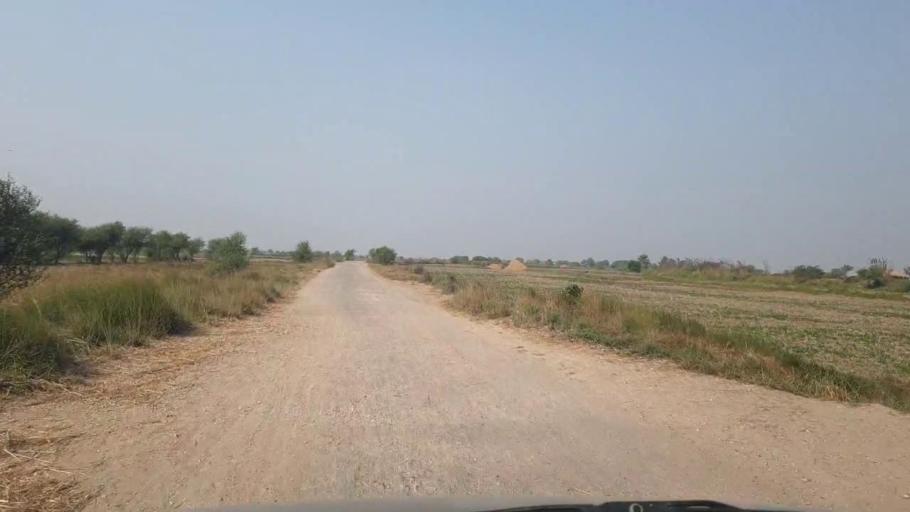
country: PK
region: Sindh
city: Tando Muhammad Khan
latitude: 25.0858
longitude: 68.3403
